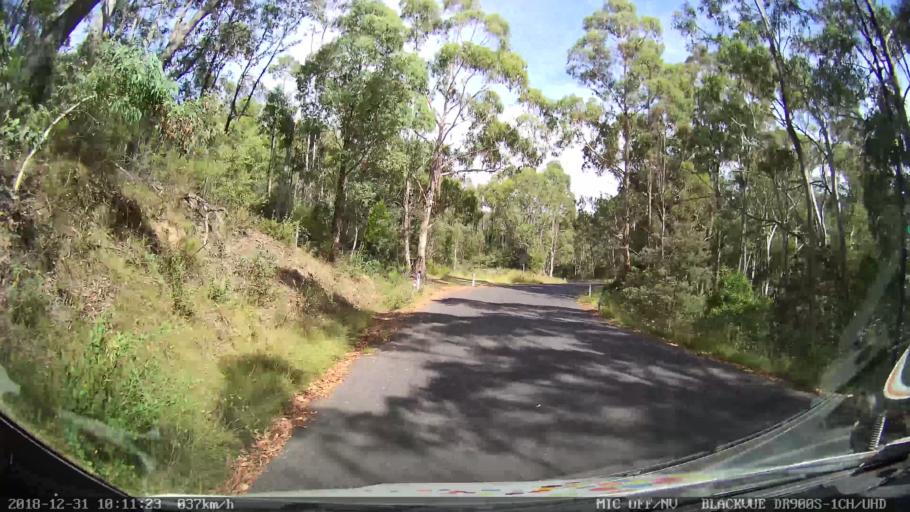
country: AU
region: New South Wales
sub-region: Snowy River
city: Jindabyne
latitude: -36.5381
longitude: 148.1674
